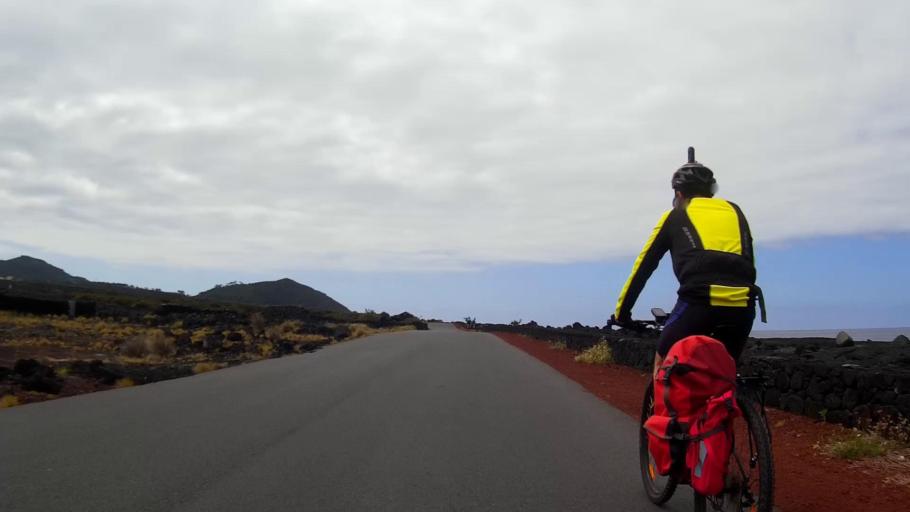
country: PT
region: Azores
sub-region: Madalena
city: Madalena
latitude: 38.5171
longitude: -28.5392
